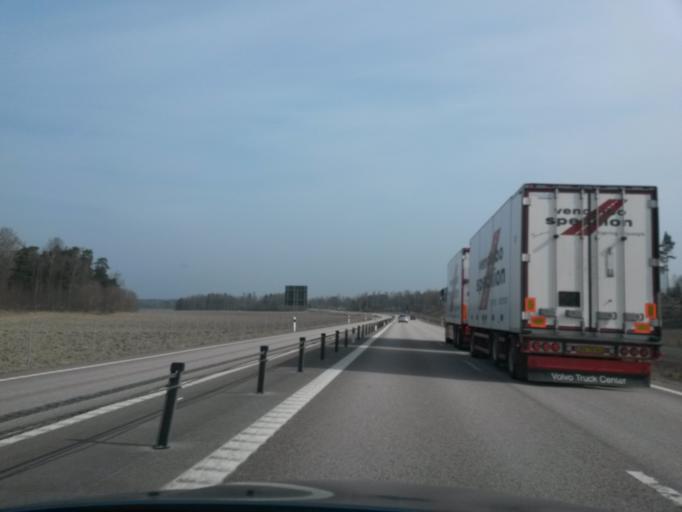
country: SE
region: Vaestra Goetaland
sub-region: Mariestads Kommun
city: Mariestad
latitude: 58.7551
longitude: 13.9634
